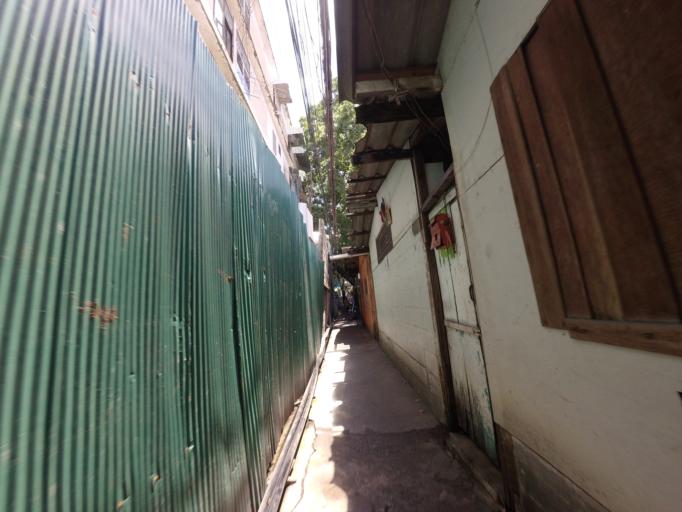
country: TH
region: Bangkok
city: Lat Phrao
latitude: 13.7989
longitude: 100.5887
